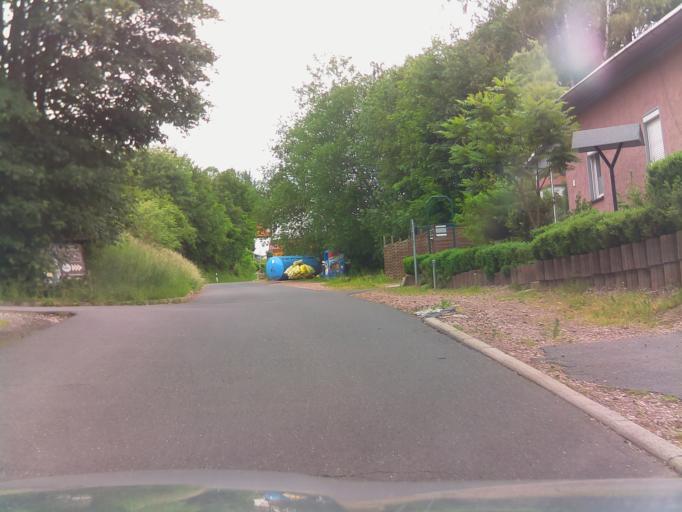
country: DE
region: Thuringia
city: Suhl
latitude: 50.6176
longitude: 10.6939
